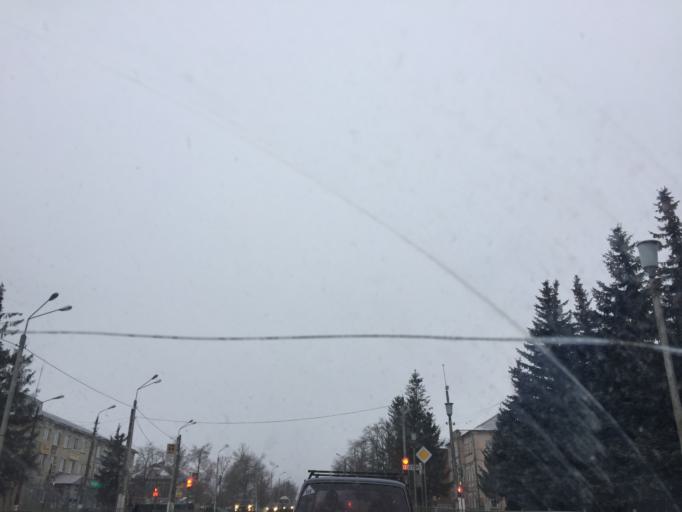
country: RU
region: Tula
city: Plavsk
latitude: 53.7068
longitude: 37.2926
